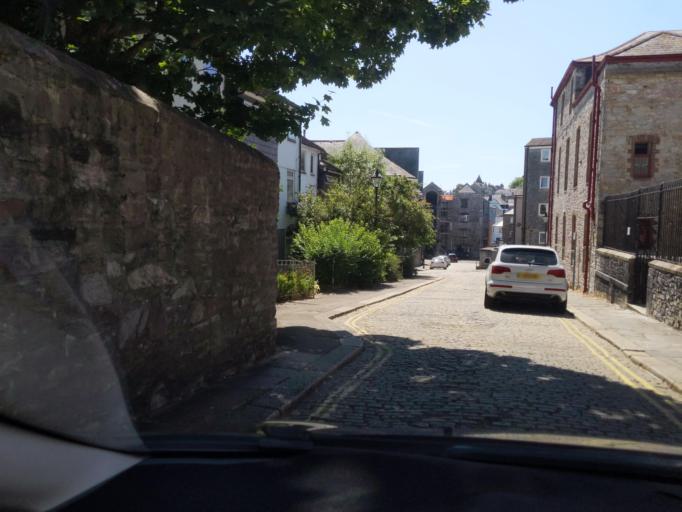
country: GB
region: England
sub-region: Plymouth
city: Plymouth
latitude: 50.3694
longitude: -4.1368
